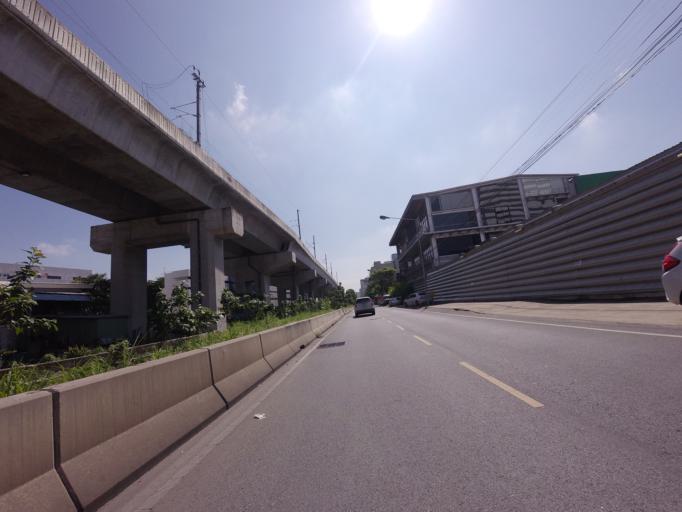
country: TH
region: Bangkok
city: Watthana
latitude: 13.7462
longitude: 100.5807
